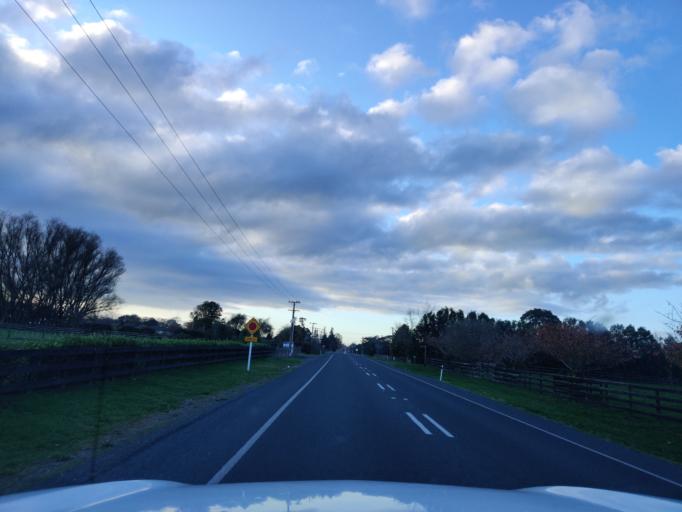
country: NZ
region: Waikato
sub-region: Waipa District
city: Cambridge
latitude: -37.8623
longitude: 175.4390
